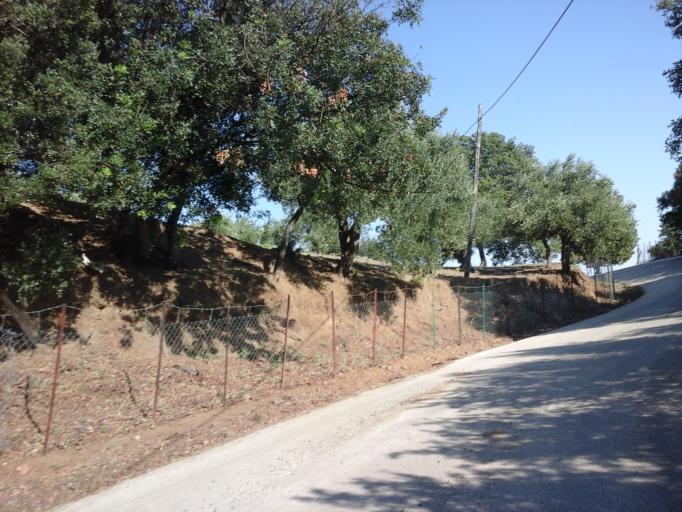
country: GR
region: East Macedonia and Thrace
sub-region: Nomos Evrou
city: Samothraki
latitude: 40.4097
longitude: 25.5684
